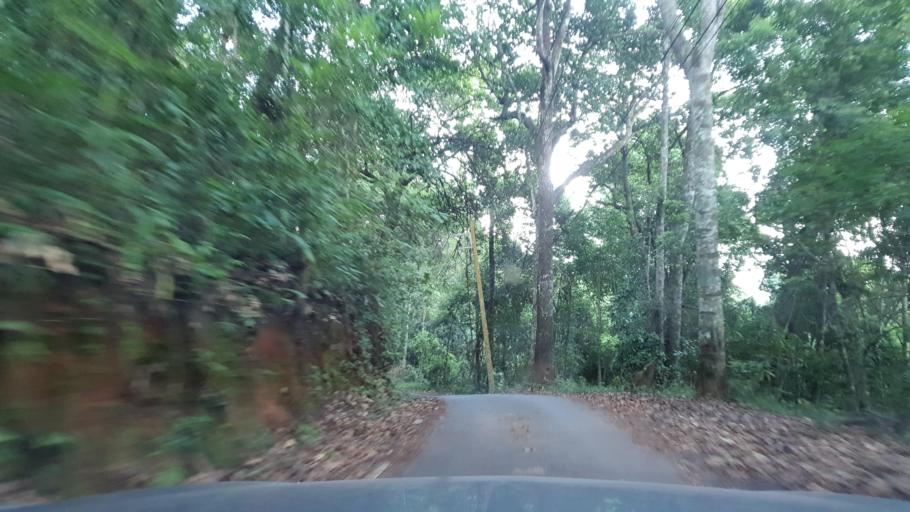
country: TH
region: Chiang Mai
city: Chiang Mai
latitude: 18.8271
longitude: 98.8962
